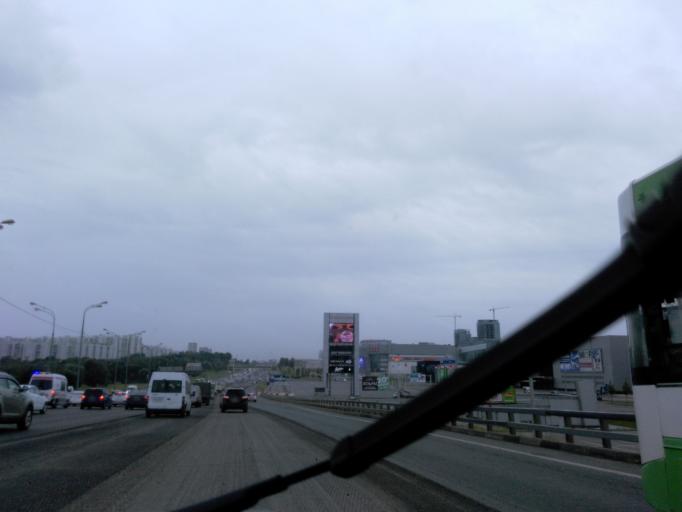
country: RU
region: Moscow
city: Strogino
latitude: 55.8269
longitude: 37.3938
